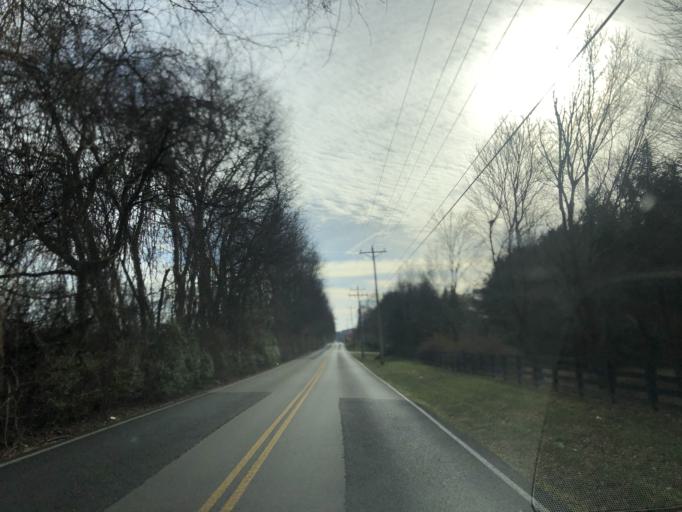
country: US
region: Tennessee
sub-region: Williamson County
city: Franklin
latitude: 35.9510
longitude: -86.9021
